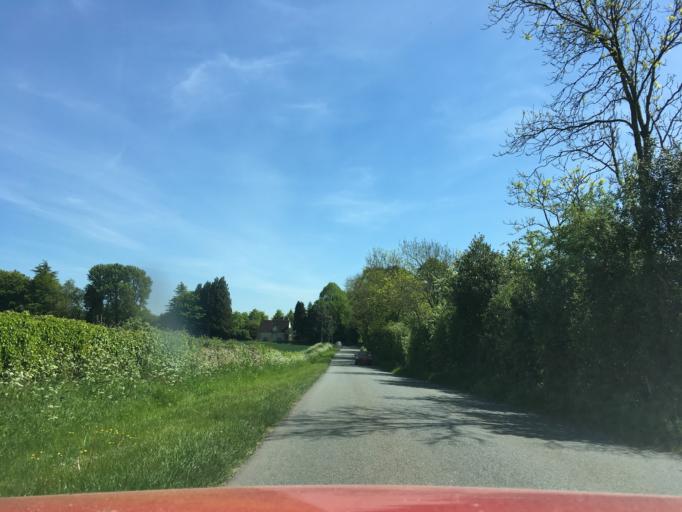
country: GB
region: England
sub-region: Gloucestershire
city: Coates
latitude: 51.7008
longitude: -2.0265
